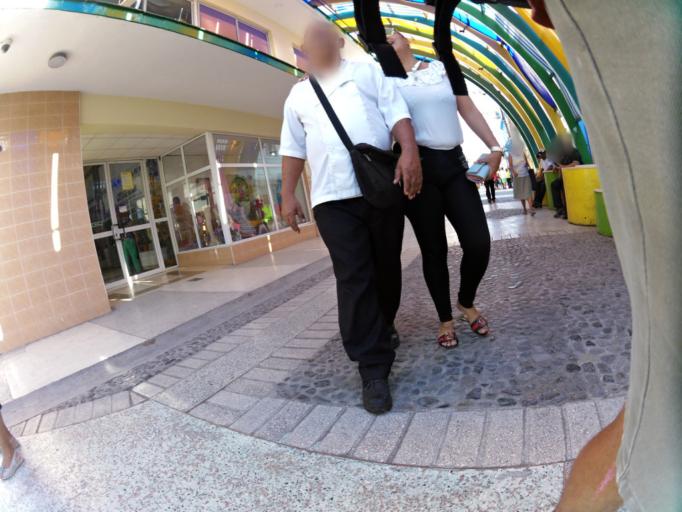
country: CU
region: Granma
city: Bayamo
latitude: 20.3715
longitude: -76.6477
